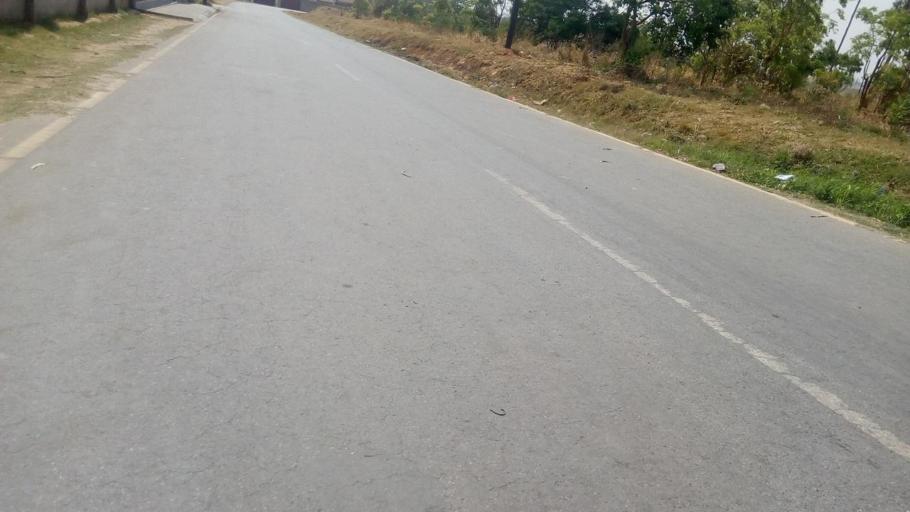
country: ZM
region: Lusaka
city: Lusaka
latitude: -15.3613
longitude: 28.2831
